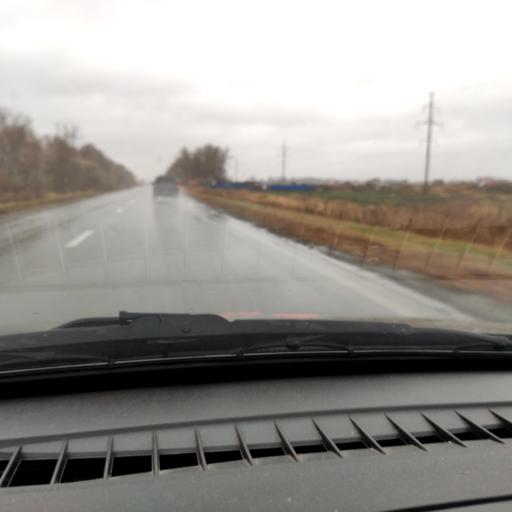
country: RU
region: Samara
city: Tol'yatti
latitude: 53.6224
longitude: 49.3085
